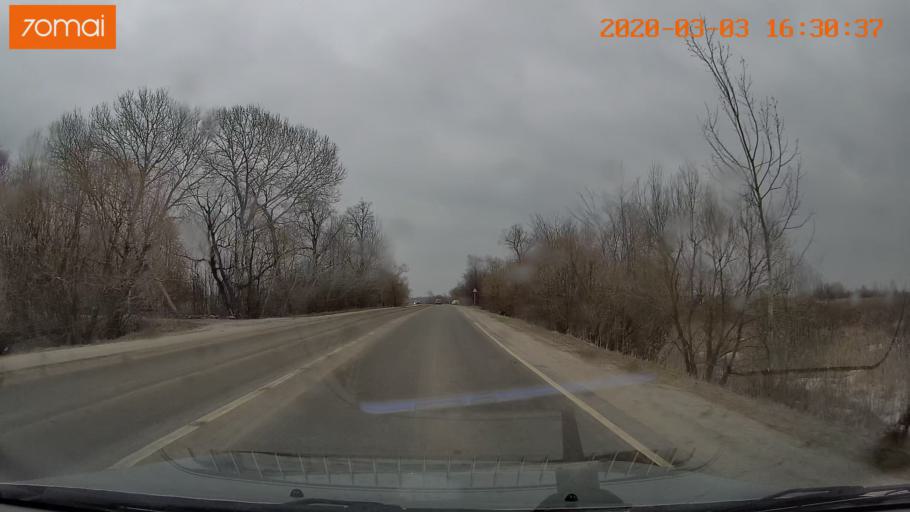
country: RU
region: Moskovskaya
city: Konobeyevo
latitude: 55.4321
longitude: 38.7132
